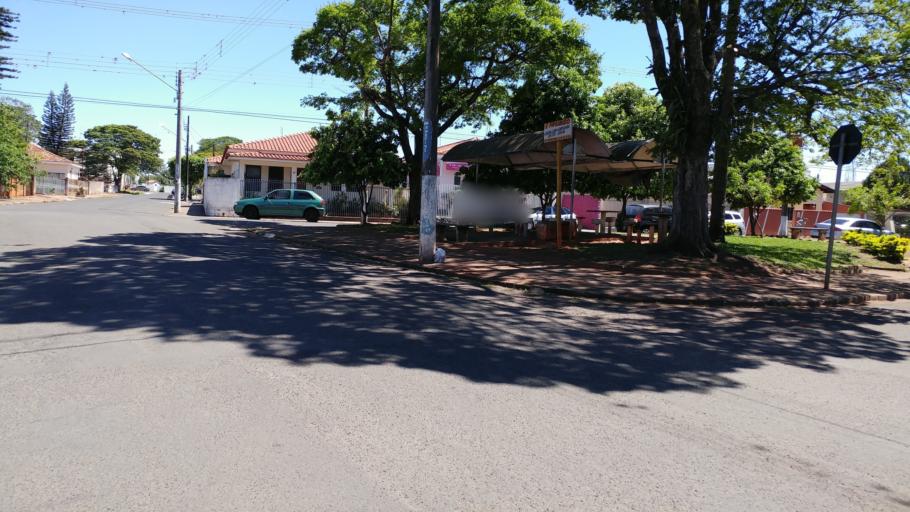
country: BR
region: Sao Paulo
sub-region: Paraguacu Paulista
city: Paraguacu Paulista
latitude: -22.4201
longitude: -50.5777
